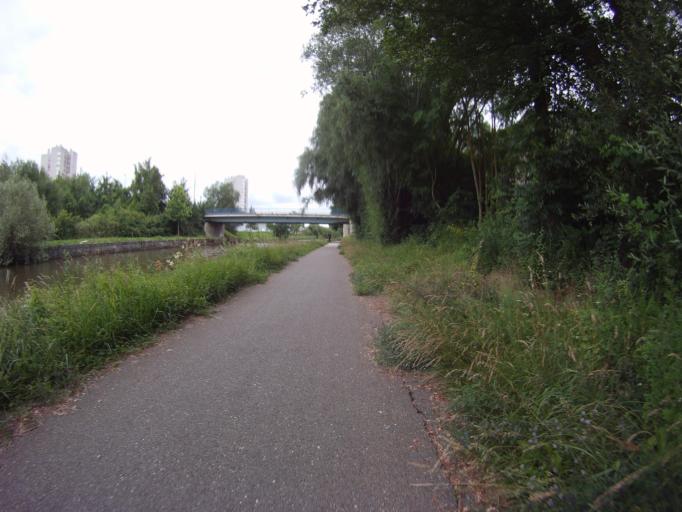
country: FR
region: Lorraine
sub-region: Departement de Meurthe-et-Moselle
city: Jarville-la-Malgrange
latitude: 48.6675
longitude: 6.2143
